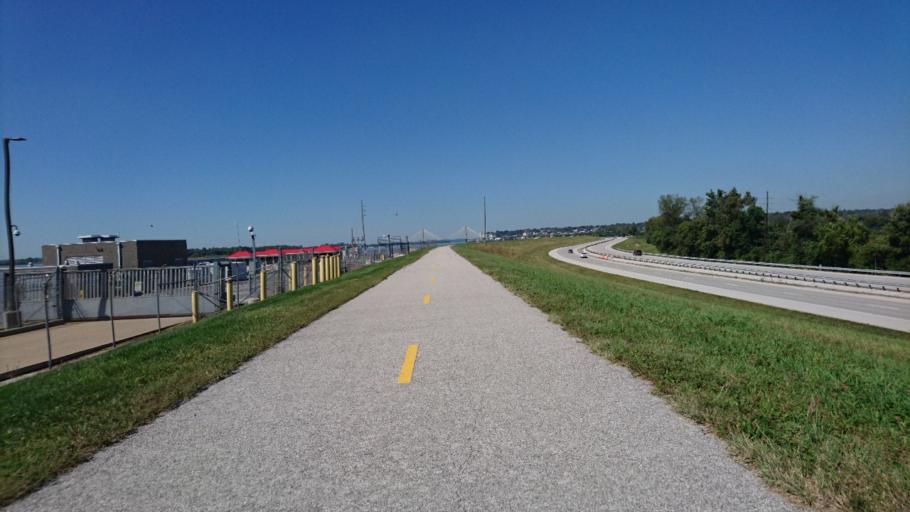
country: US
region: Illinois
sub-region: Madison County
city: Alton
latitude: 38.8717
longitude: -90.1511
